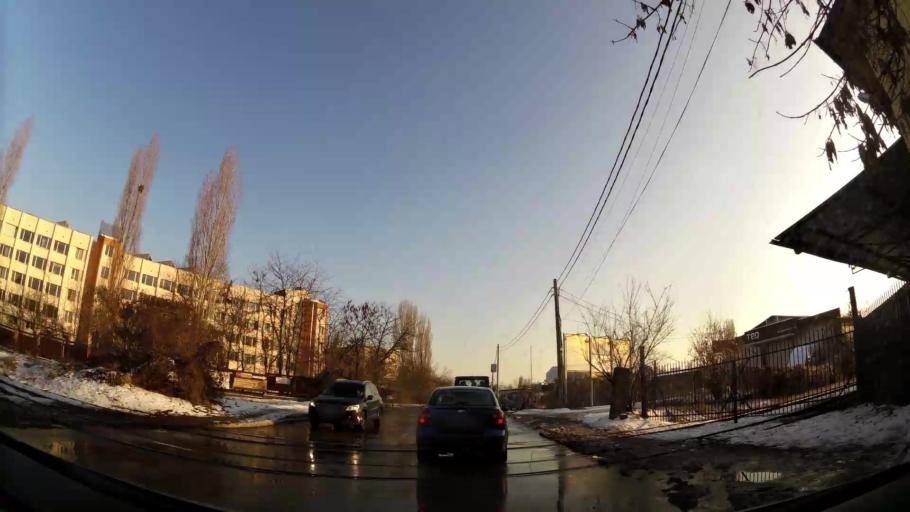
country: BG
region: Sofia-Capital
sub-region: Stolichna Obshtina
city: Sofia
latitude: 42.6780
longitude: 23.3788
